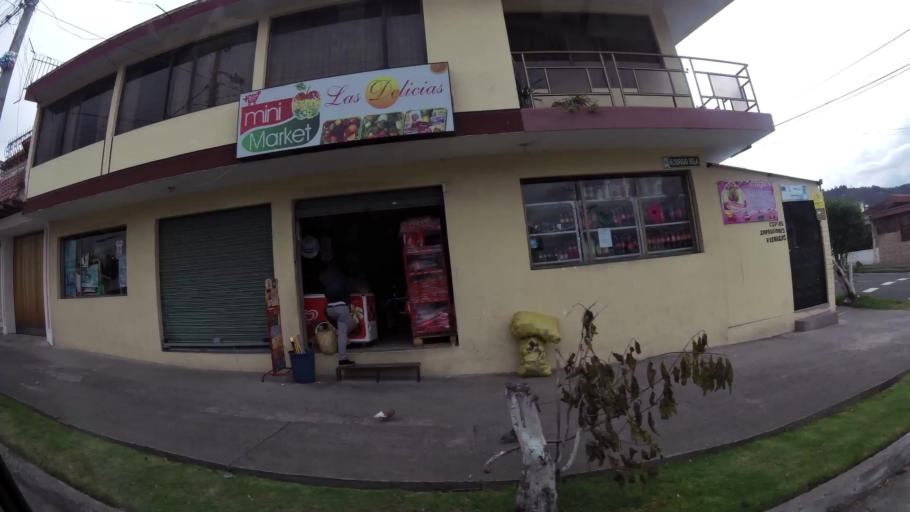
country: EC
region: Tungurahua
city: Ambato
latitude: -1.2600
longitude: -78.6313
